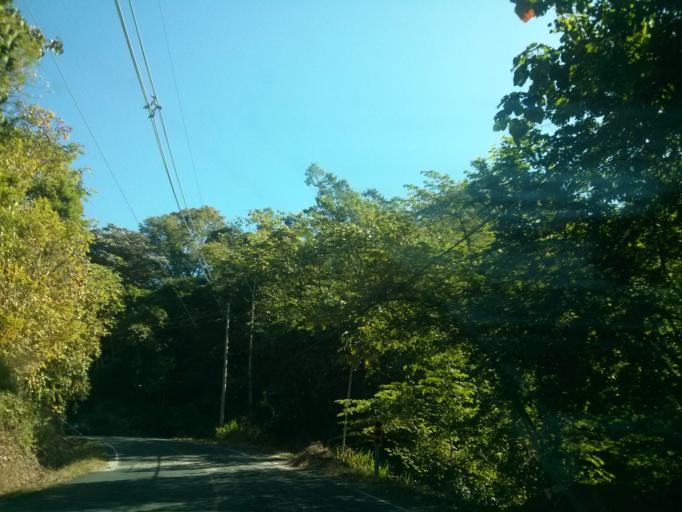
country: CR
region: Puntarenas
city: Paquera
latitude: 9.7726
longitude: -84.9693
